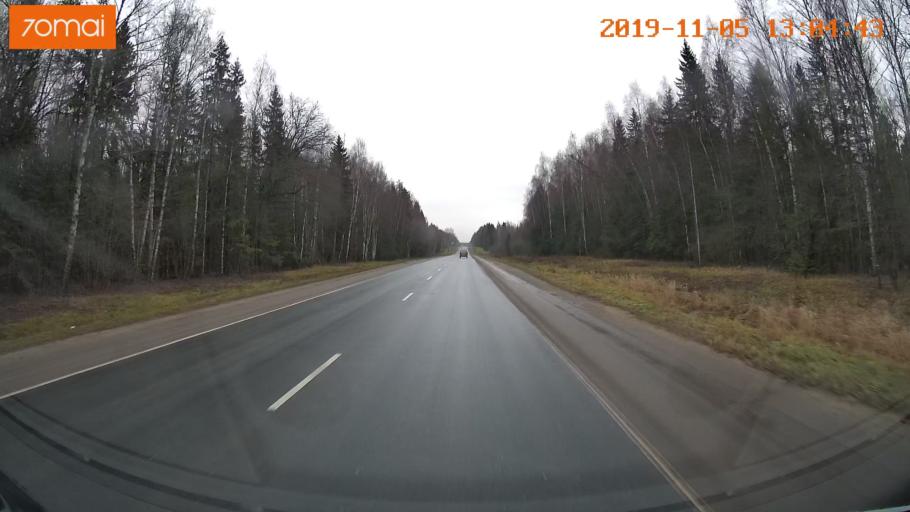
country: RU
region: Ivanovo
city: Kitovo
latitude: 56.8872
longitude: 41.2273
